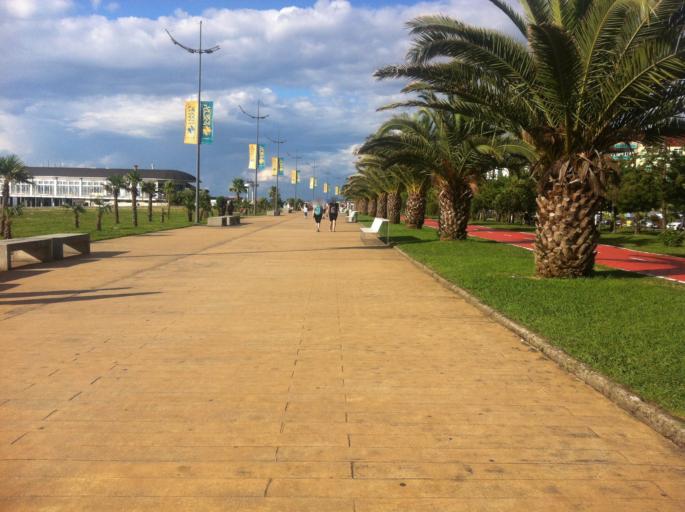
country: GE
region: Ajaria
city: Batumi
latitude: 41.6450
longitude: 41.6169
